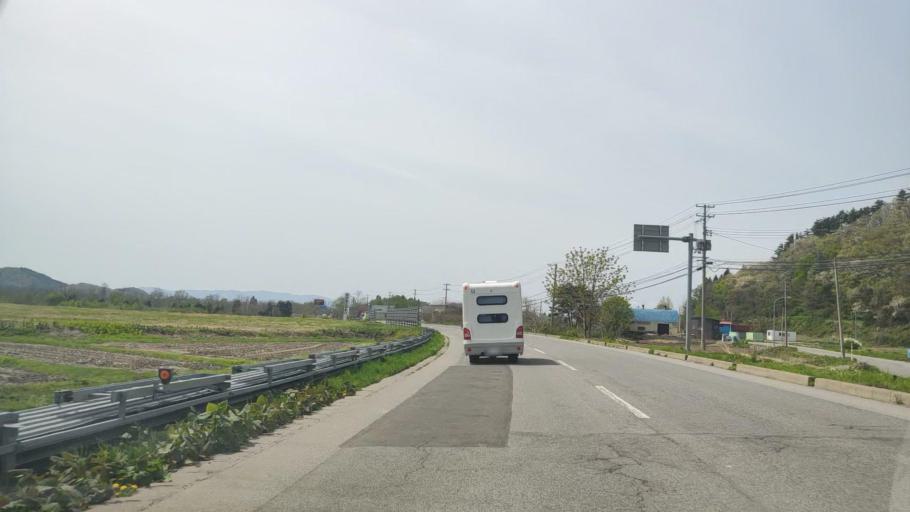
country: JP
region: Aomori
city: Aomori Shi
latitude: 40.8303
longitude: 140.8491
